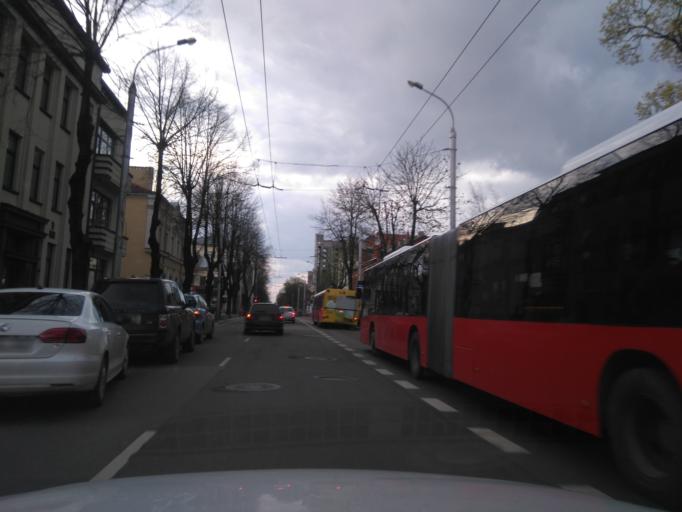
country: LT
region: Kauno apskritis
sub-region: Kaunas
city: Kaunas
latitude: 54.8953
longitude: 23.9232
